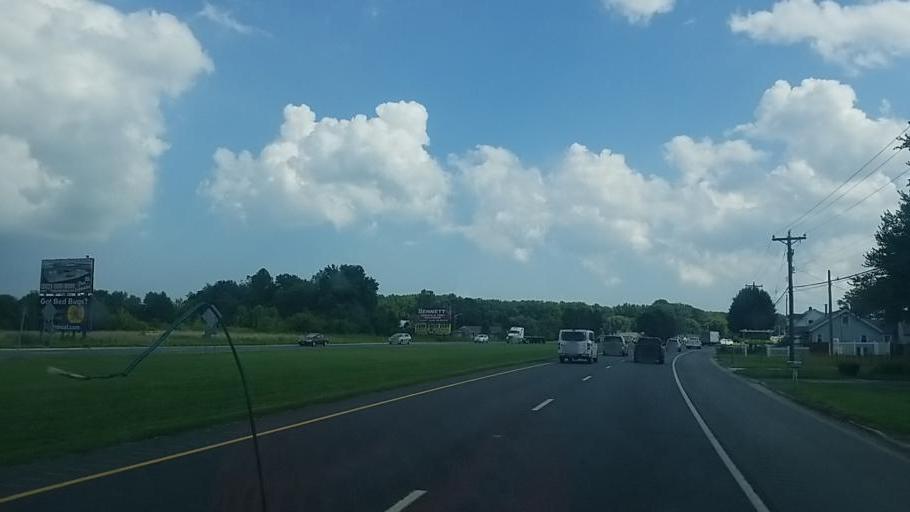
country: US
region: Delaware
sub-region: Sussex County
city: Selbyville
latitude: 38.5169
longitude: -75.2399
